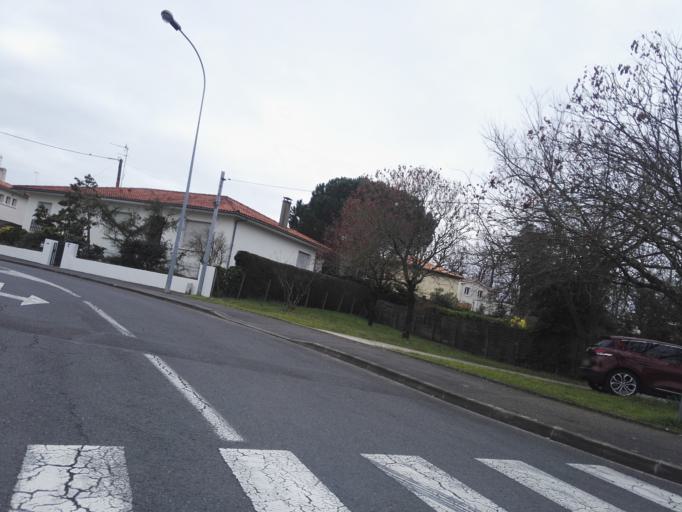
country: FR
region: Aquitaine
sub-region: Departement de la Gironde
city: Talence
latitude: 44.8022
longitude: -0.5838
